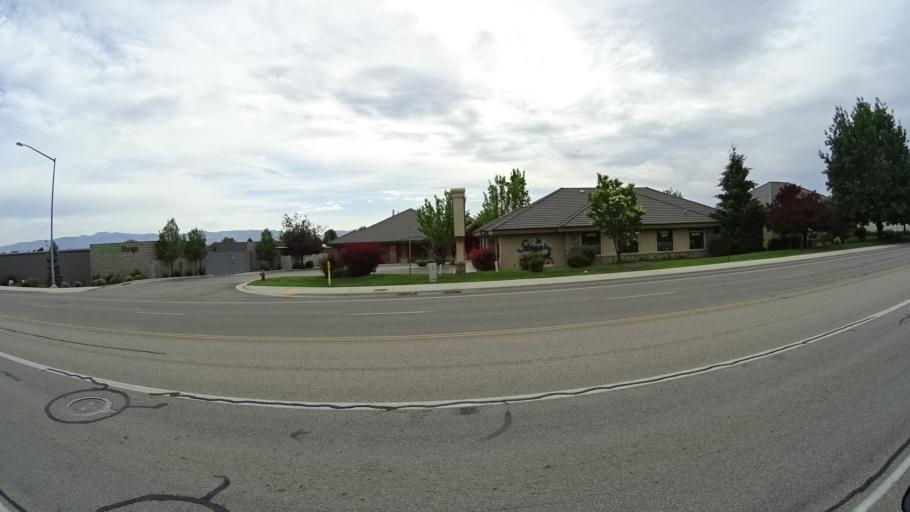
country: US
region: Idaho
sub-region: Ada County
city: Meridian
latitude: 43.5808
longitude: -116.3546
